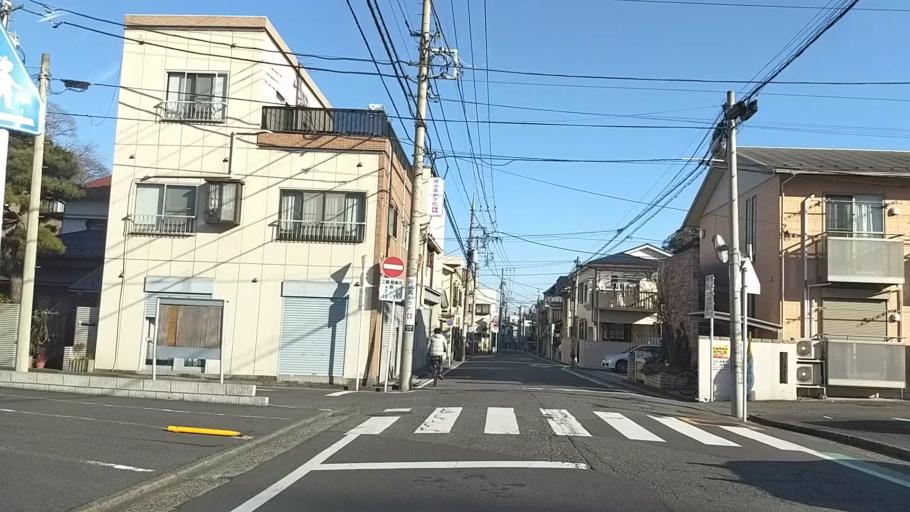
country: JP
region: Kanagawa
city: Yokohama
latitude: 35.4255
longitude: 139.6115
